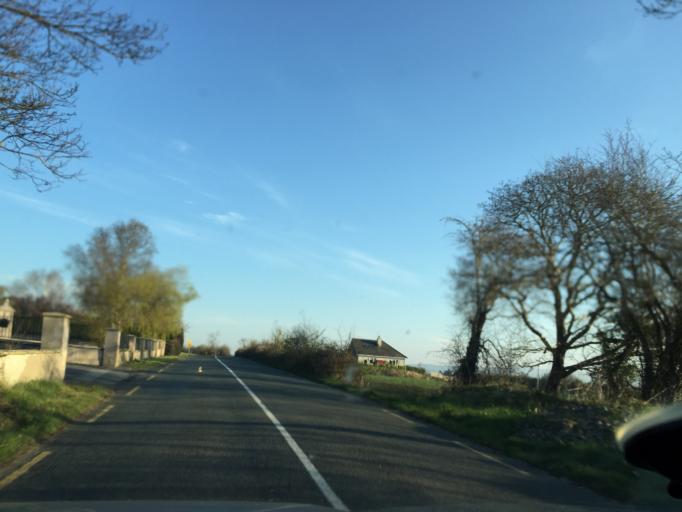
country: IE
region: Munster
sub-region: Ciarrai
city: Cill Airne
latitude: 52.0836
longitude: -9.5260
